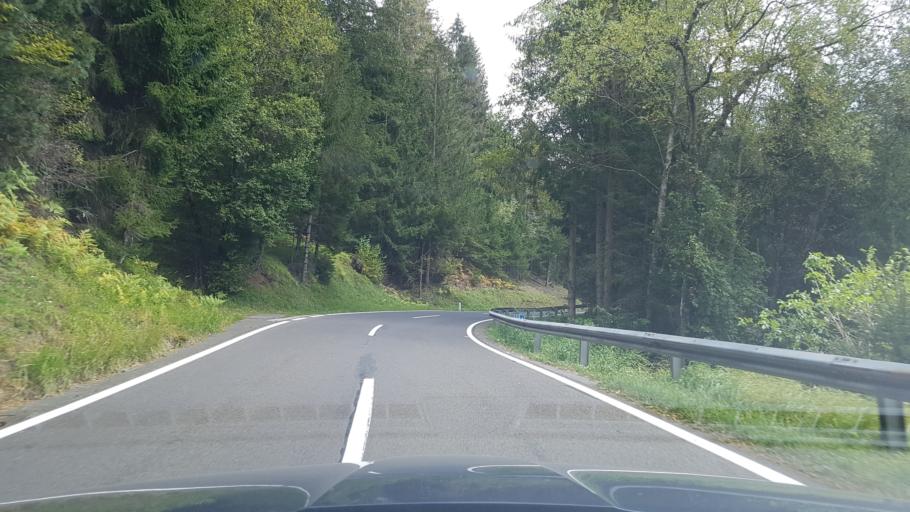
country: AT
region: Styria
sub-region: Politischer Bezirk Murtal
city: Grosslobming
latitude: 47.1575
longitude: 14.7905
